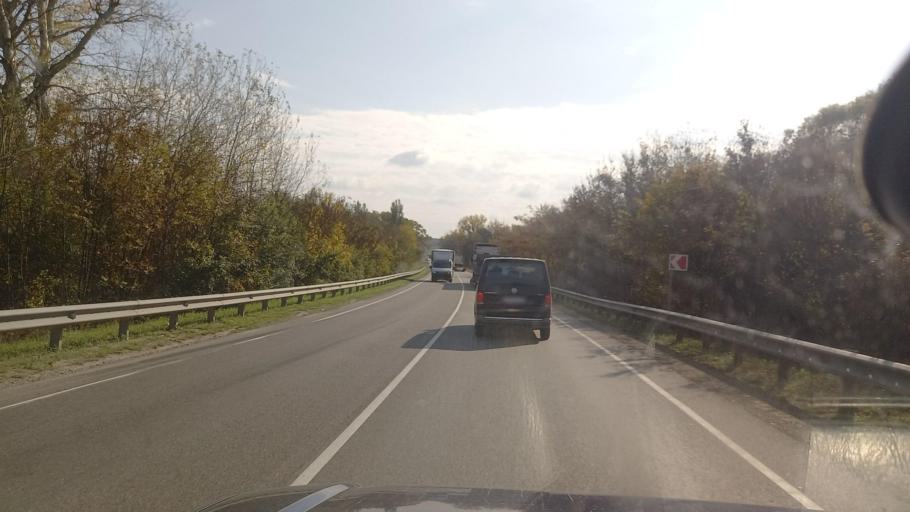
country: RU
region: Krasnodarskiy
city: Abinsk
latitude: 44.8447
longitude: 38.1524
